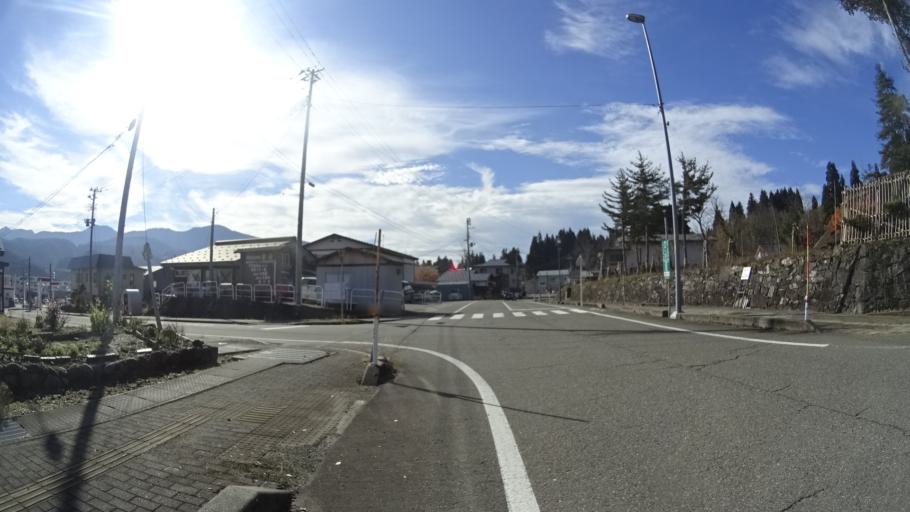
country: JP
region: Niigata
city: Tochio-honcho
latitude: 37.3217
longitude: 139.0163
